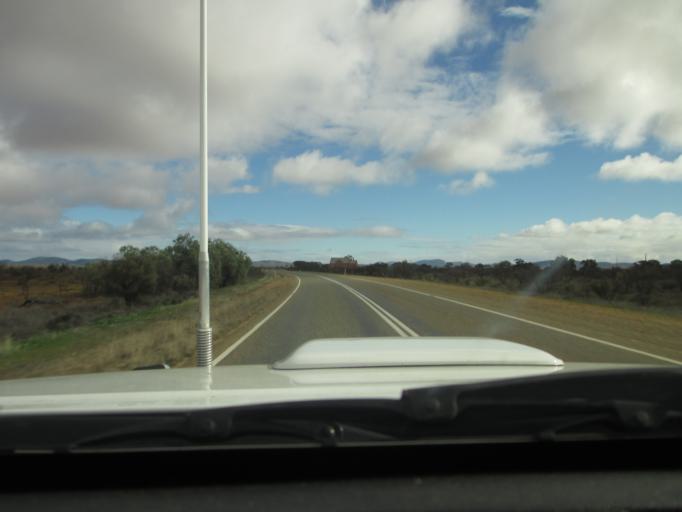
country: AU
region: South Australia
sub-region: Flinders Ranges
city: Quorn
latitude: -32.0747
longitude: 138.4991
